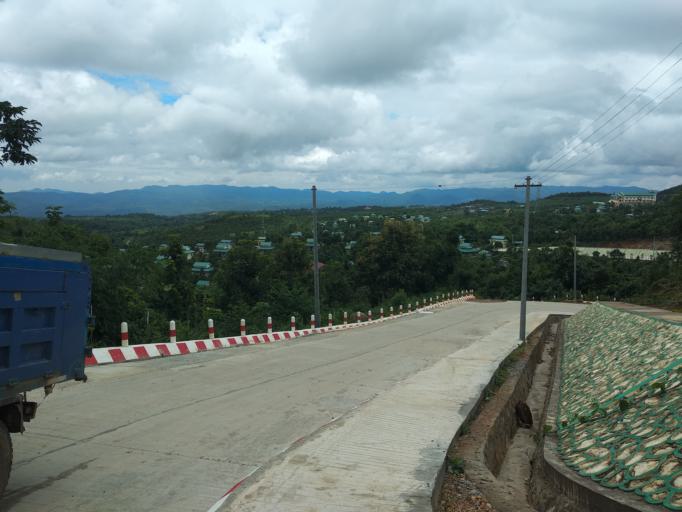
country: MM
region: Mandalay
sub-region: Pyin Oo Lwin District
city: Pyin Oo Lwin
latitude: 21.9084
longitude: 96.3872
